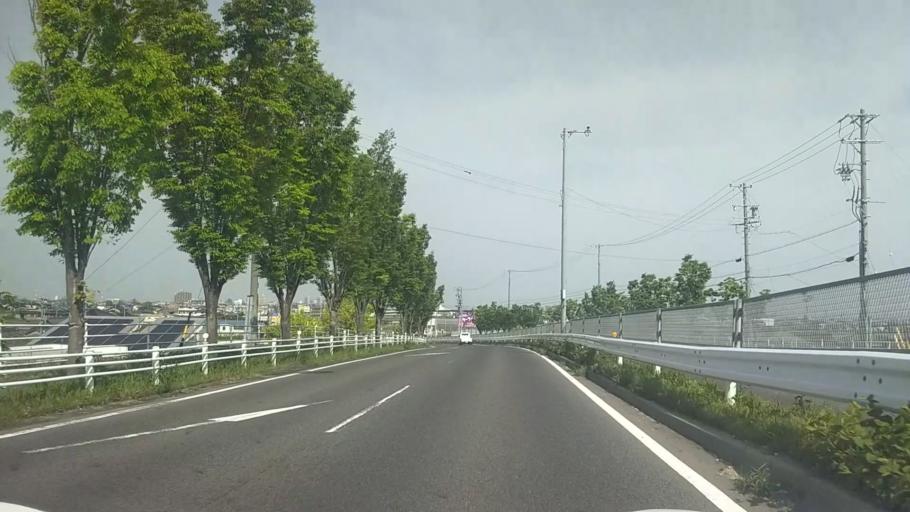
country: JP
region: Aichi
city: Okazaki
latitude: 34.9387
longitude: 137.1394
